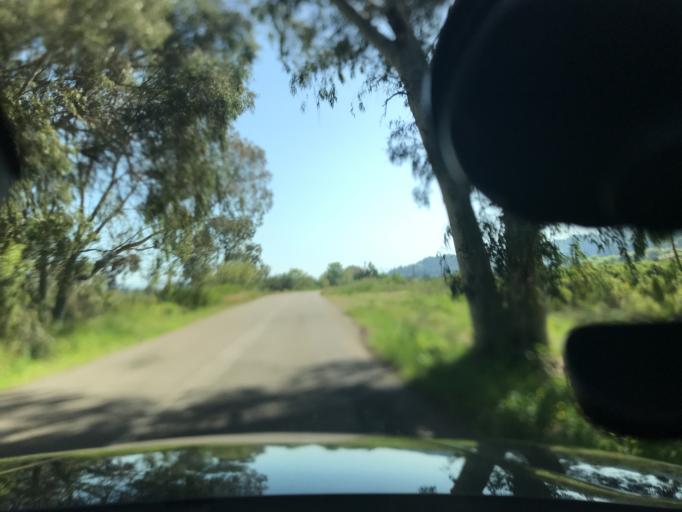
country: GR
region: West Greece
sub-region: Nomos Ileias
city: Epitalion
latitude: 37.6398
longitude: 21.4853
